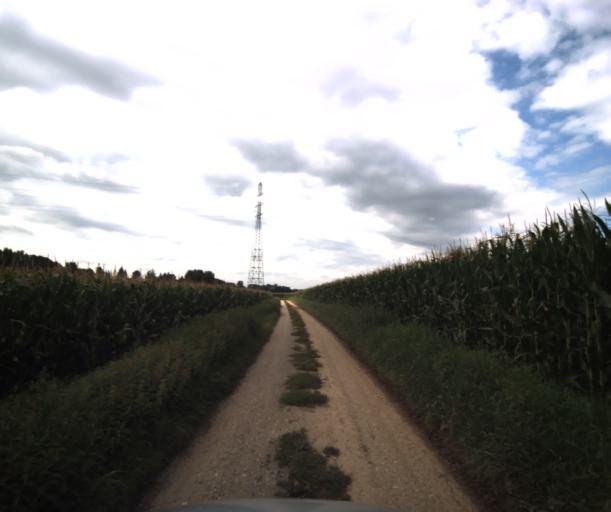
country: FR
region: Midi-Pyrenees
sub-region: Departement de la Haute-Garonne
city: Longages
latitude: 43.3823
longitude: 1.2313
